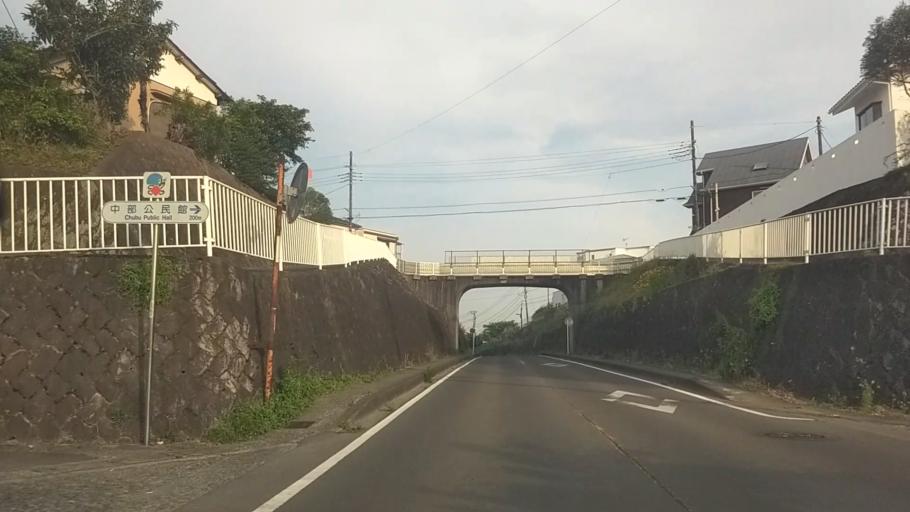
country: JP
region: Kanagawa
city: Odawara
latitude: 35.3124
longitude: 139.1172
